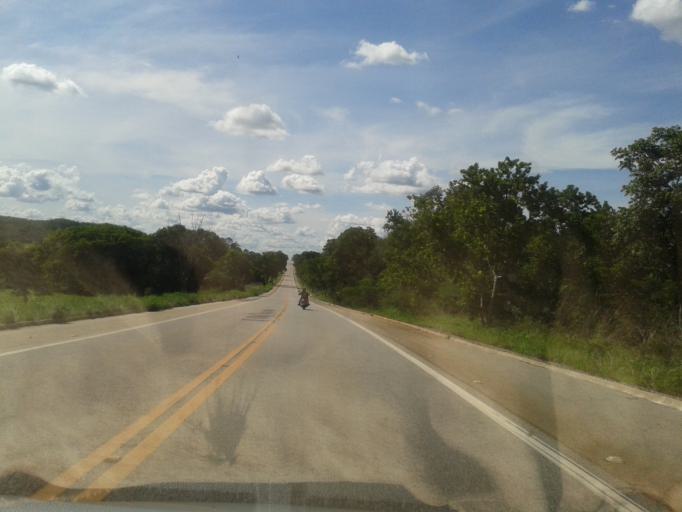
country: BR
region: Goias
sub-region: Itapirapua
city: Itapirapua
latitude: -15.3032
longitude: -50.4466
